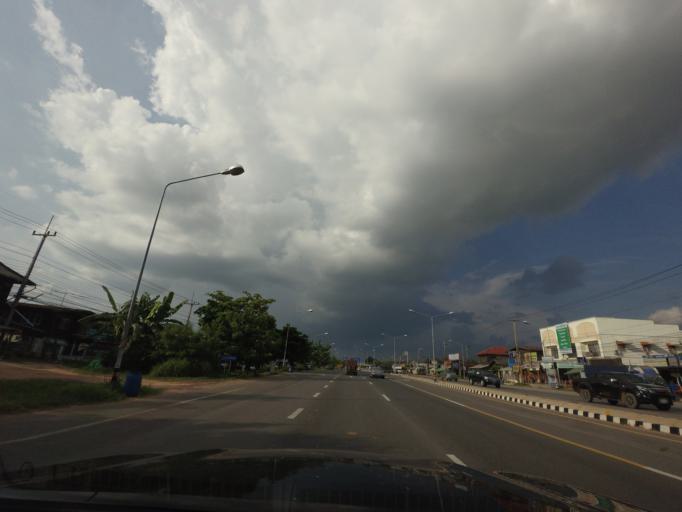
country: TH
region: Khon Kaen
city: Khon Kaen
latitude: 16.3233
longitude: 102.7959
